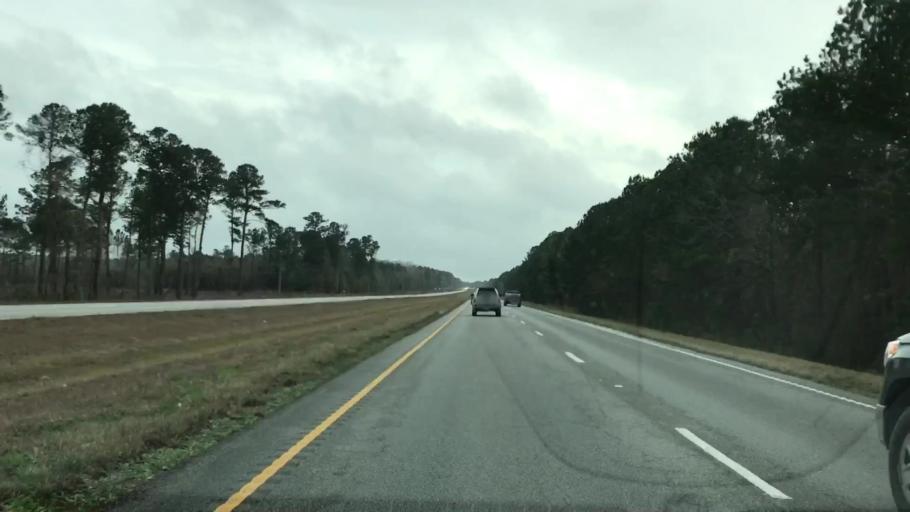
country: US
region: South Carolina
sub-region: Berkeley County
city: Goose Creek
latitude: 33.0850
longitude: -80.0323
